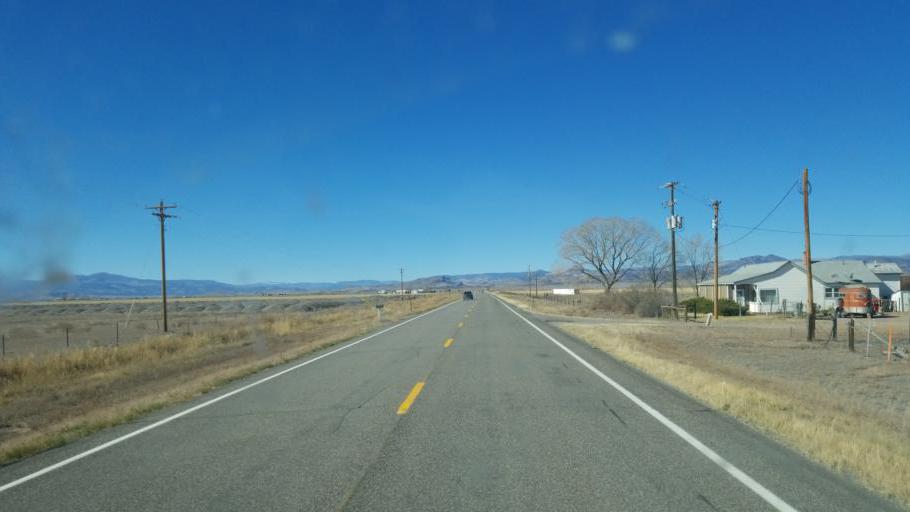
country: US
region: Colorado
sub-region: Saguache County
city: Center
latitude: 37.7482
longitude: -106.1922
